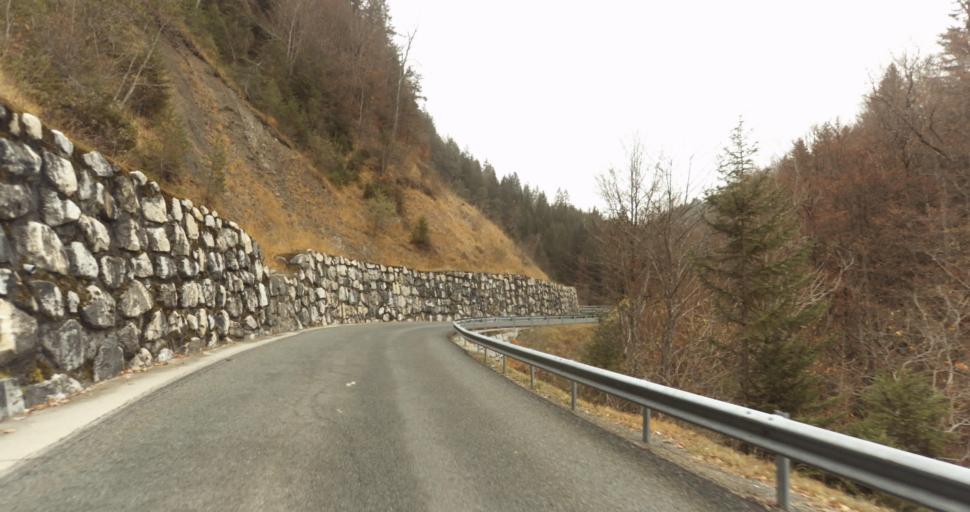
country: FR
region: Rhone-Alpes
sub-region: Departement de la Haute-Savoie
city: Doussard
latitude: 45.7892
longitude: 6.2583
